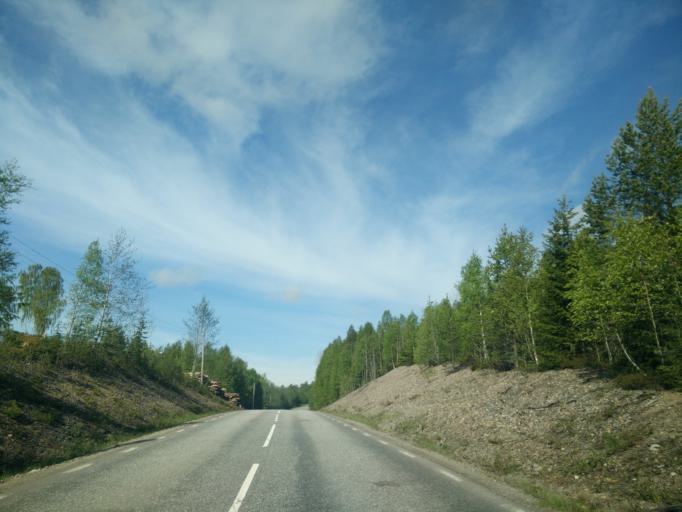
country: SE
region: Vaesternorrland
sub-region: Sundsvalls Kommun
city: Nolby
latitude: 62.3031
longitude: 17.3070
